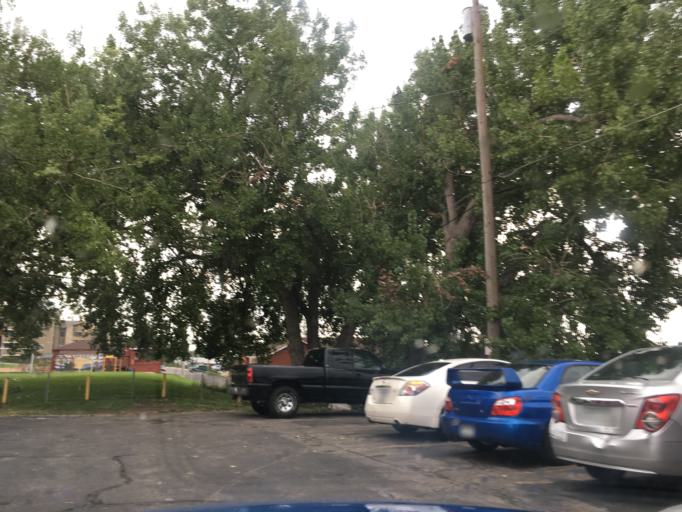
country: US
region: Colorado
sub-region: Arapahoe County
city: Sheridan
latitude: 39.6570
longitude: -105.0267
